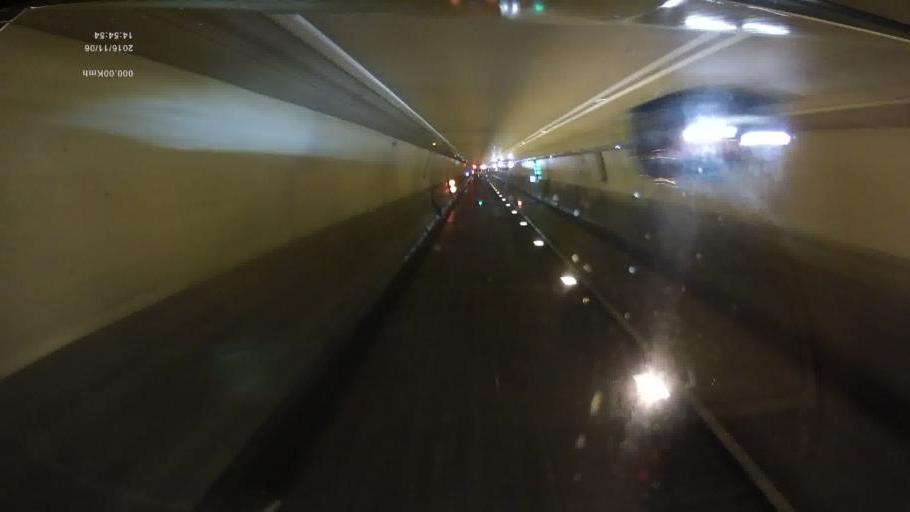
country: SK
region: Kosicky
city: Krompachy
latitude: 49.0017
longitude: 20.8833
